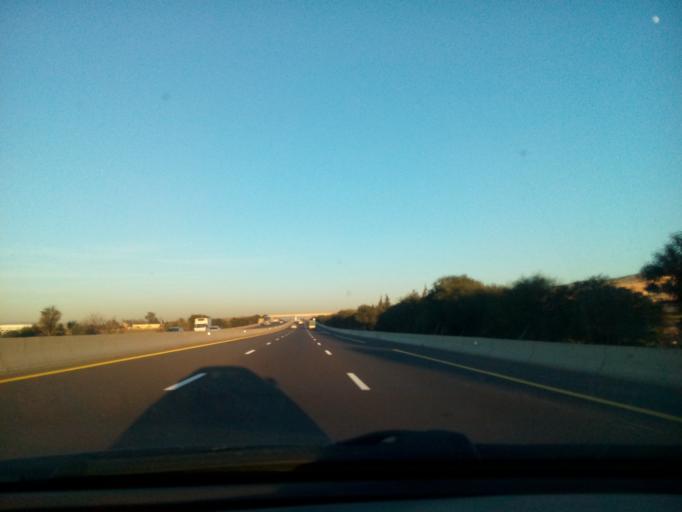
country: DZ
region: Relizane
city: Oued Rhiou
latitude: 36.0007
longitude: 1.0014
